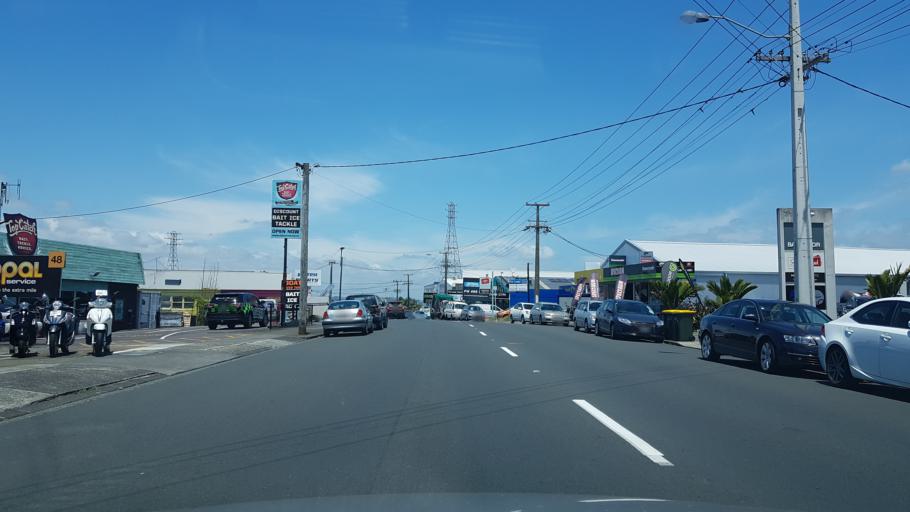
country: NZ
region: Auckland
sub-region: Auckland
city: North Shore
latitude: -36.7939
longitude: 174.7652
